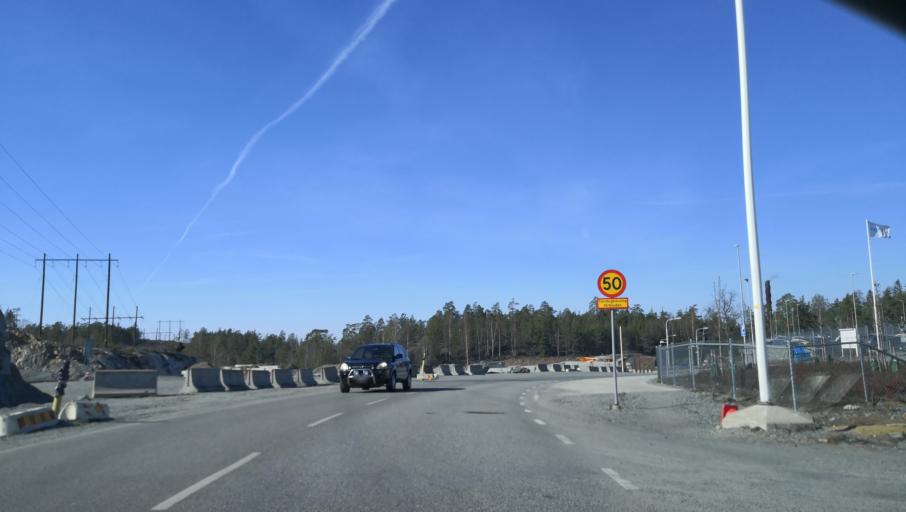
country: SE
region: Stockholm
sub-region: Varmdo Kommun
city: Gustavsberg
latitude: 59.3090
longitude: 18.3813
